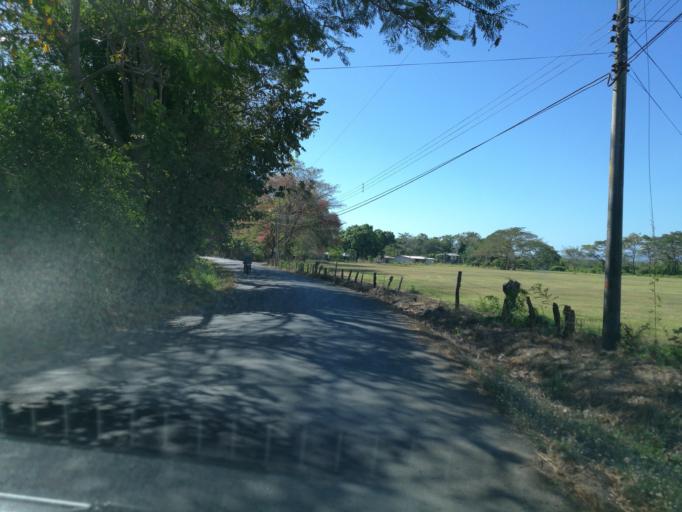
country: CR
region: Puntarenas
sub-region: Canton Central de Puntarenas
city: Puntarenas
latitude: 10.0888
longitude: -84.9531
